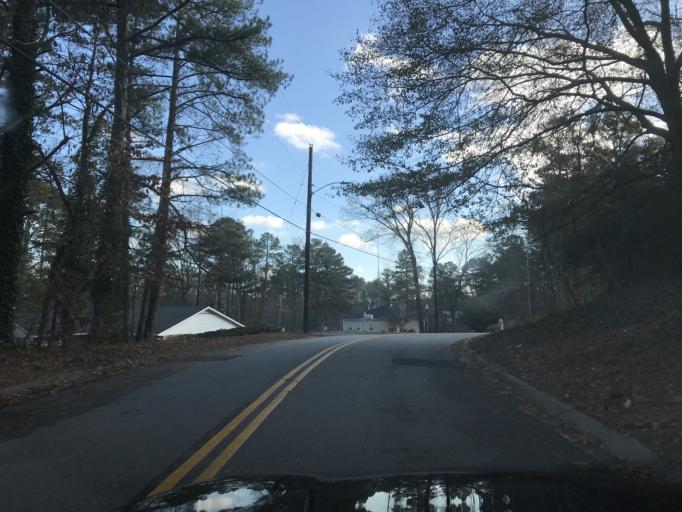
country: US
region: Georgia
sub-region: Fulton County
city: College Park
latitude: 33.6401
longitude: -84.4734
